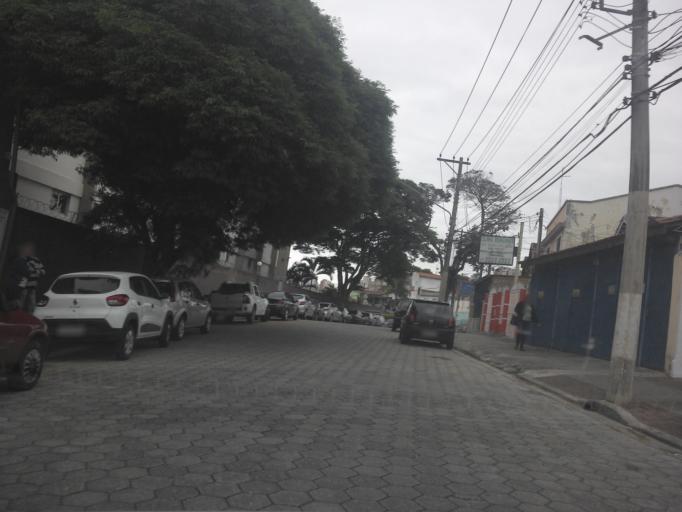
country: BR
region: Sao Paulo
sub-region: Sao Jose Dos Campos
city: Sao Jose dos Campos
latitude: -23.1855
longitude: -45.8799
